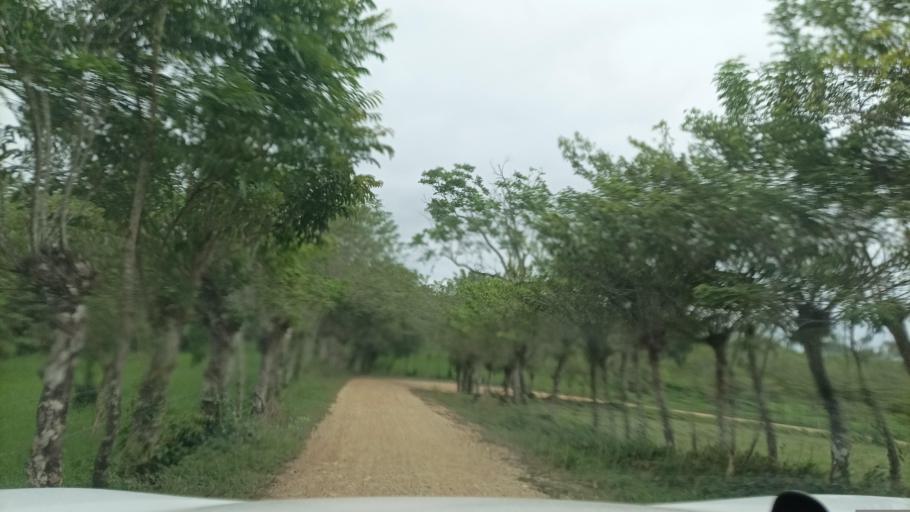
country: MX
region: Veracruz
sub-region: Uxpanapa
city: Poblado Cinco
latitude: 17.5023
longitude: -94.5637
